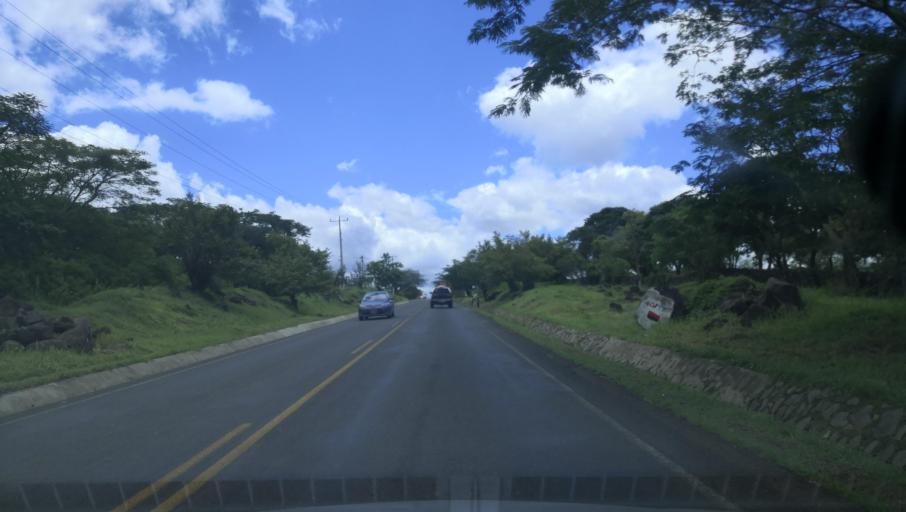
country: NI
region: Esteli
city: Esteli
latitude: 13.1947
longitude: -86.3731
